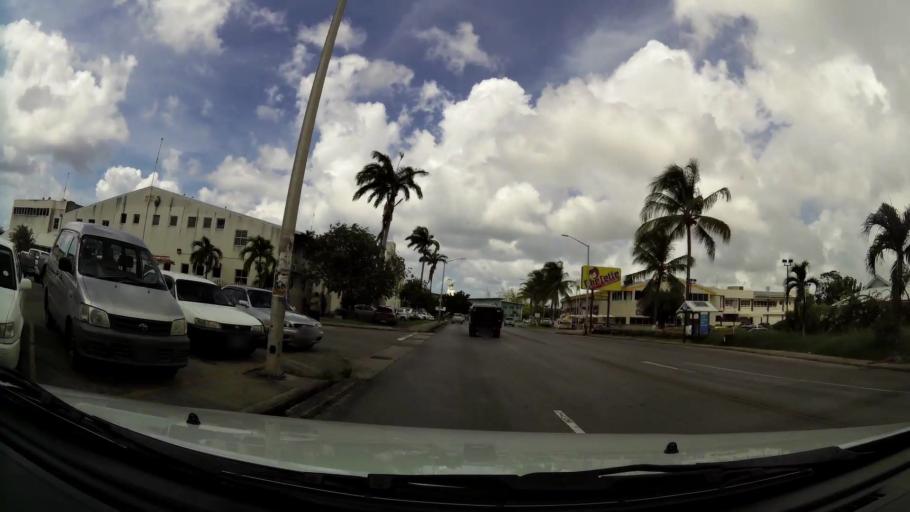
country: BB
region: Saint Michael
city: Bridgetown
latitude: 13.0997
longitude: -59.6243
